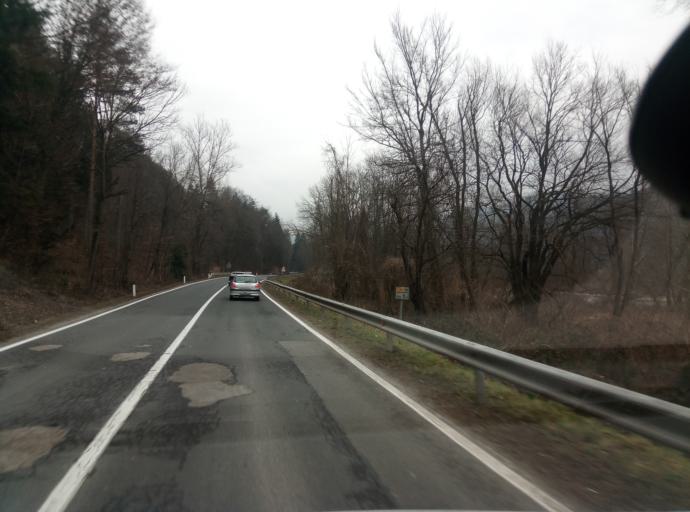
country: SI
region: Moravce
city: Moravce
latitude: 46.0908
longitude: 14.7000
